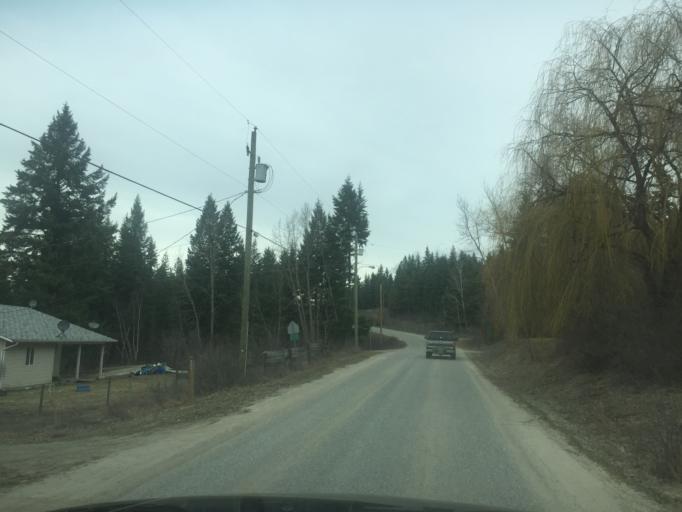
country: CA
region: British Columbia
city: Kamloops
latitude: 51.3185
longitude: -120.1479
